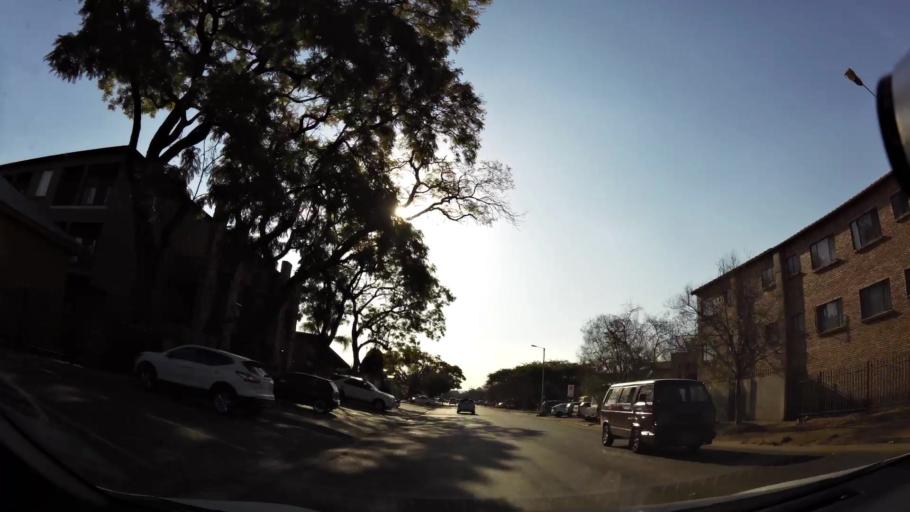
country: ZA
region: North-West
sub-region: Bojanala Platinum District Municipality
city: Rustenburg
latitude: -25.6720
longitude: 27.2355
